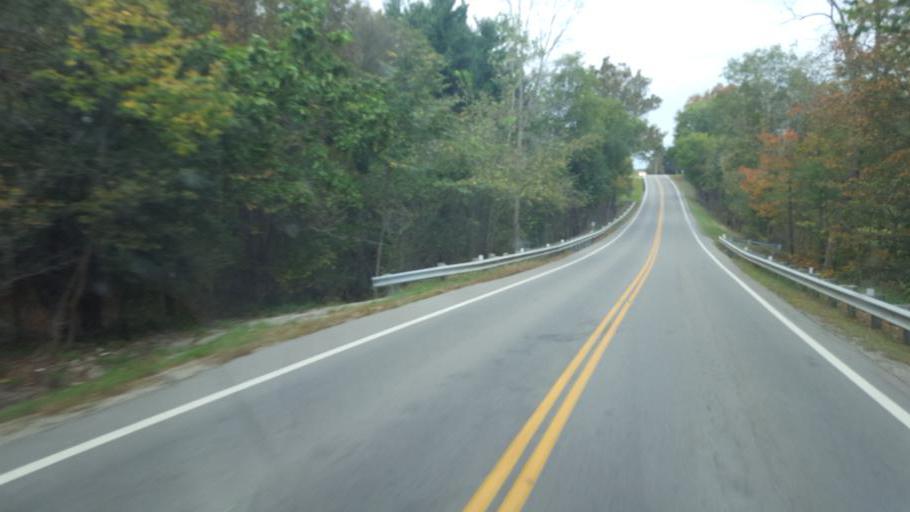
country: US
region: Ohio
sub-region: Huron County
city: Wakeman
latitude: 41.2438
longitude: -82.3955
